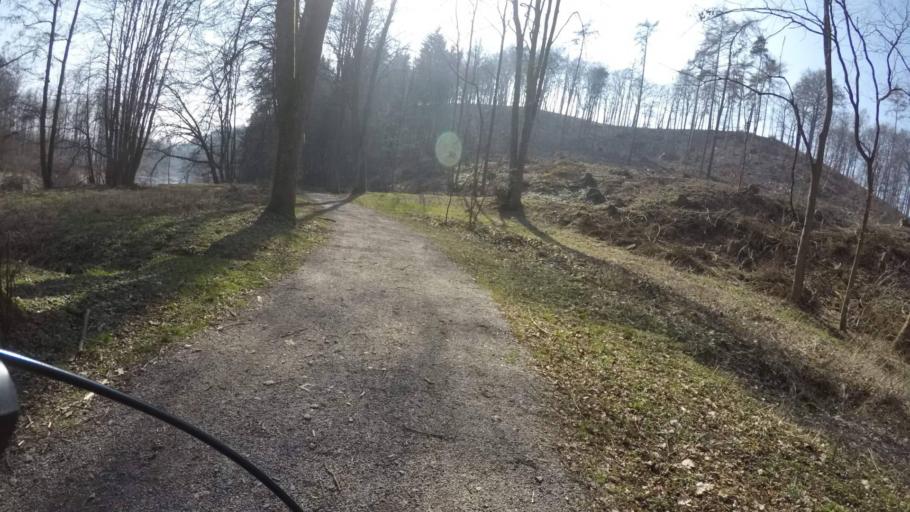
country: DE
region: Saxony
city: Penig
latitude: 50.9125
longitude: 12.6740
